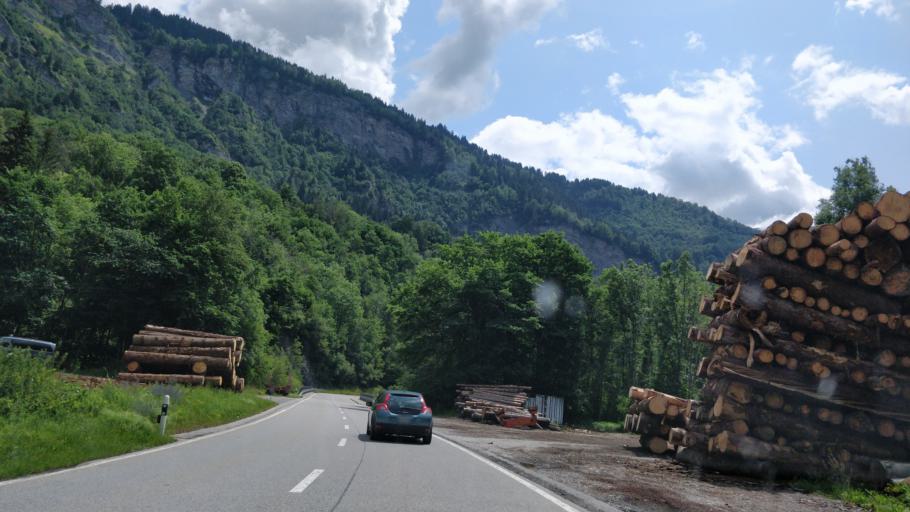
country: CH
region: Grisons
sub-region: Surselva District
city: Ilanz
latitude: 46.7567
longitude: 9.2131
